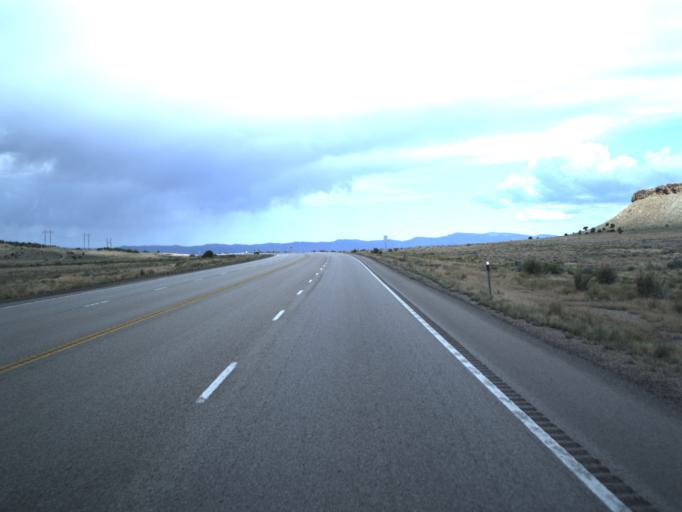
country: US
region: Utah
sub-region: Carbon County
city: Wellington
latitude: 39.5438
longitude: -110.6152
